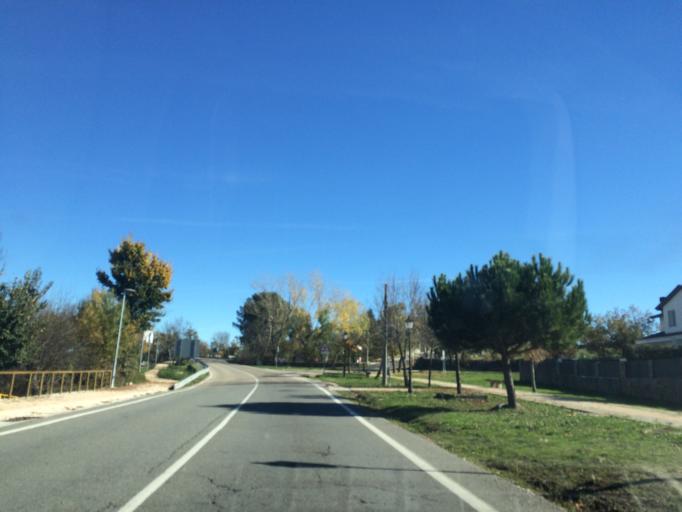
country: ES
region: Madrid
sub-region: Provincia de Madrid
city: Boalo
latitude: 40.7154
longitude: -3.9139
